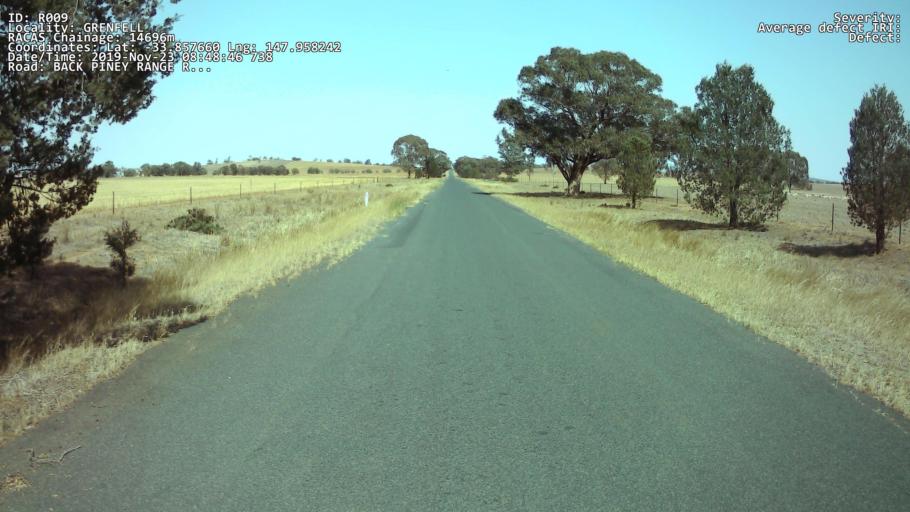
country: AU
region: New South Wales
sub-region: Weddin
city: Grenfell
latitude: -33.8577
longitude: 147.9582
